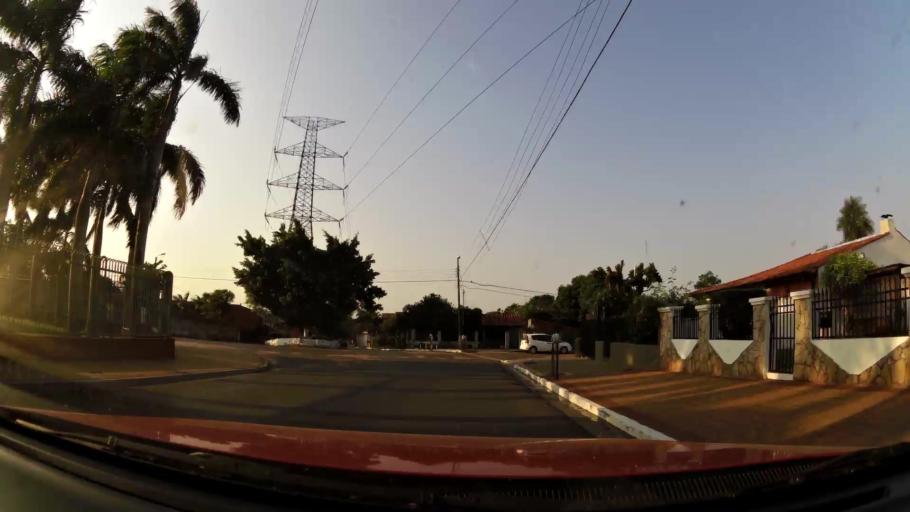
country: PY
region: Central
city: Lambare
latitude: -25.3487
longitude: -57.6097
